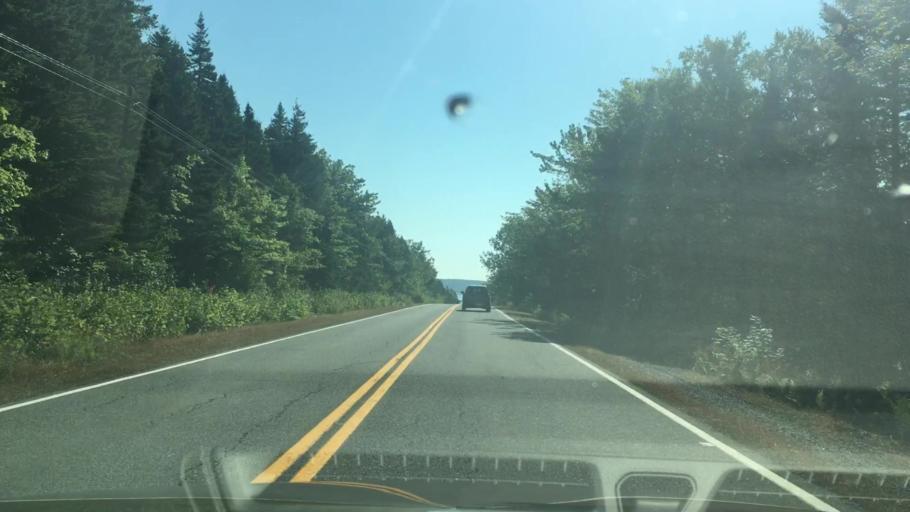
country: CA
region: Nova Scotia
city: Cole Harbour
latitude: 44.8159
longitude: -62.8789
